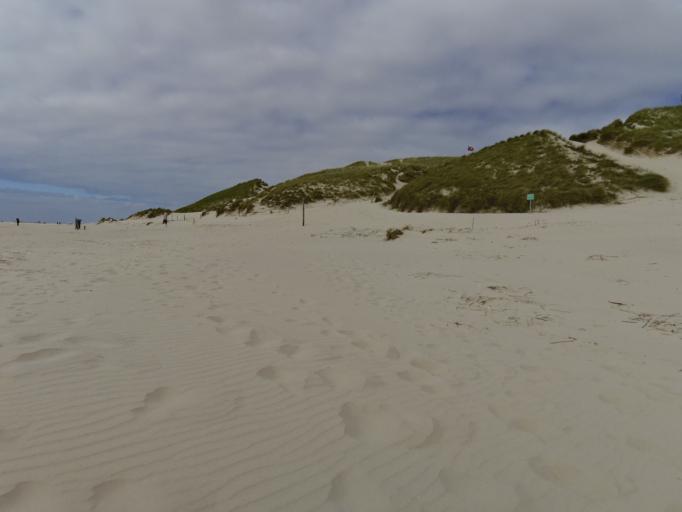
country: DE
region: Schleswig-Holstein
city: Nebel
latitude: 54.6255
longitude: 8.3519
